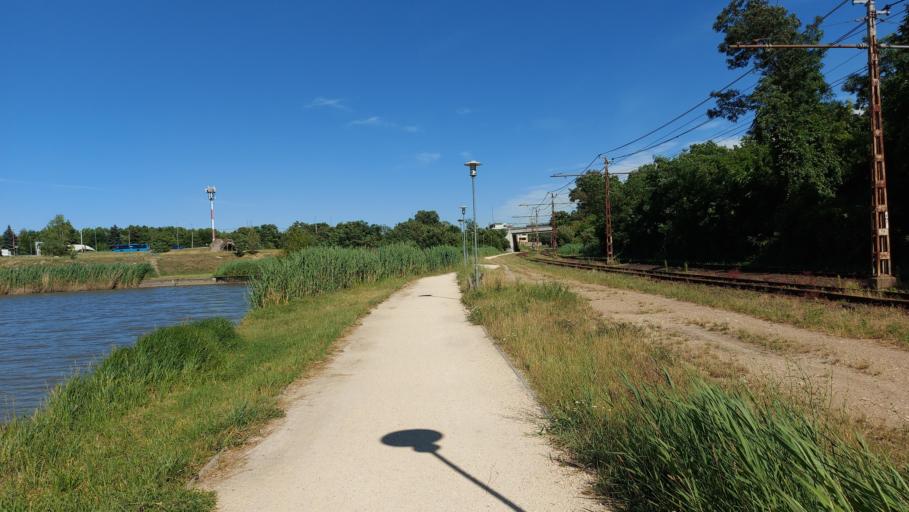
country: HU
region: Budapest
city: Budapest XXII. keruelet
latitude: 47.4453
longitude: 19.0023
